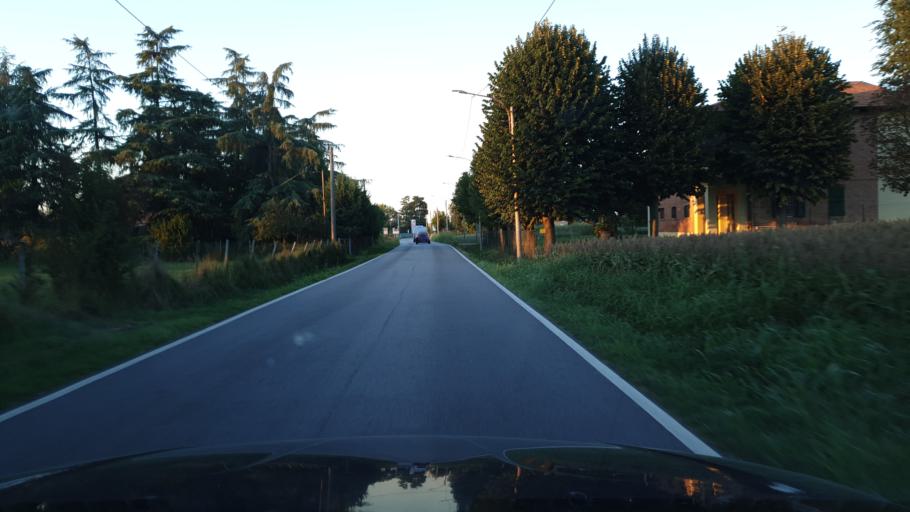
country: IT
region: Emilia-Romagna
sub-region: Provincia di Bologna
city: Quarto Inferiore
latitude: 44.5397
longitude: 11.3935
